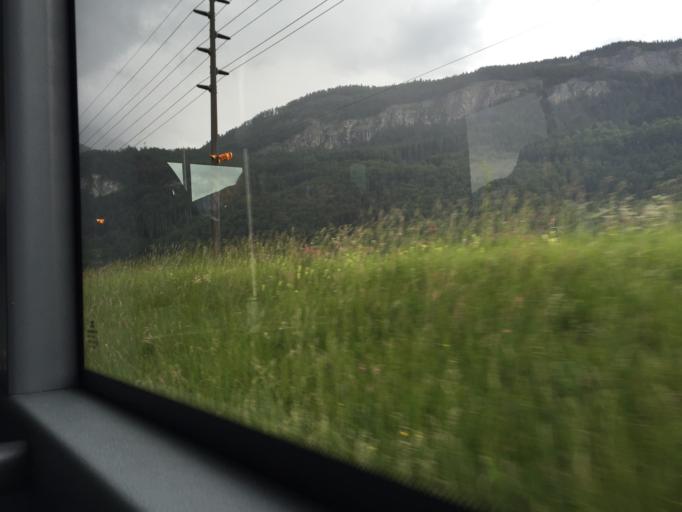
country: CH
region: Bern
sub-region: Interlaken-Oberhasli District
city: Meiringen
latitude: 46.7388
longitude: 8.1509
